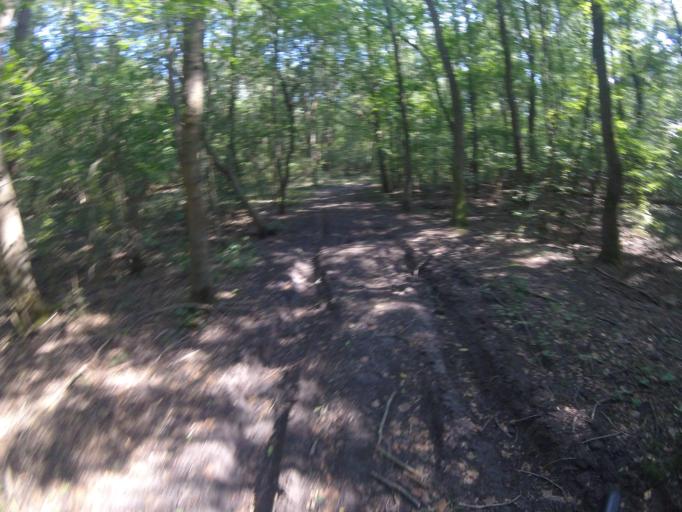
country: HU
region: Nograd
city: Bujak
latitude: 47.8967
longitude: 19.5372
